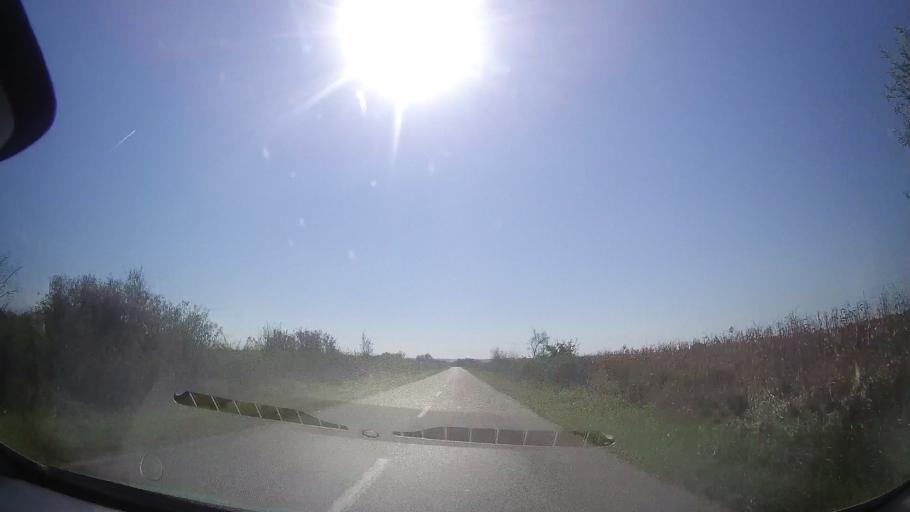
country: RO
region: Timis
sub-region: Comuna Bethausen
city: Bethausen
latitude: 45.8247
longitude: 21.9597
